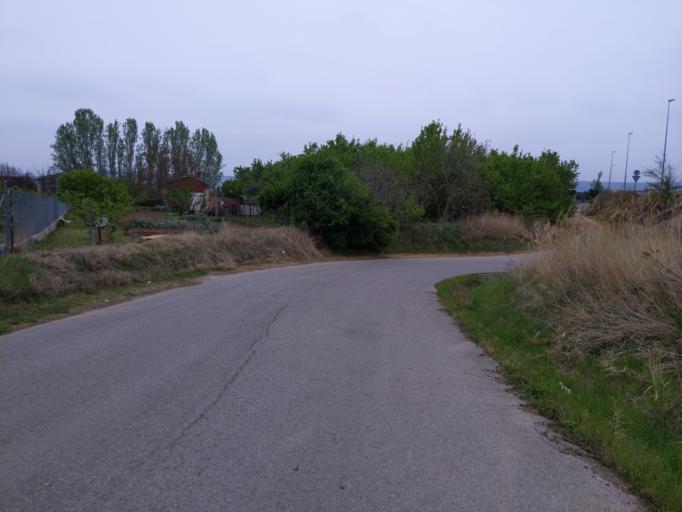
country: ES
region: La Rioja
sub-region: Provincia de La Rioja
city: Lardero
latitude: 42.4141
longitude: -2.4669
